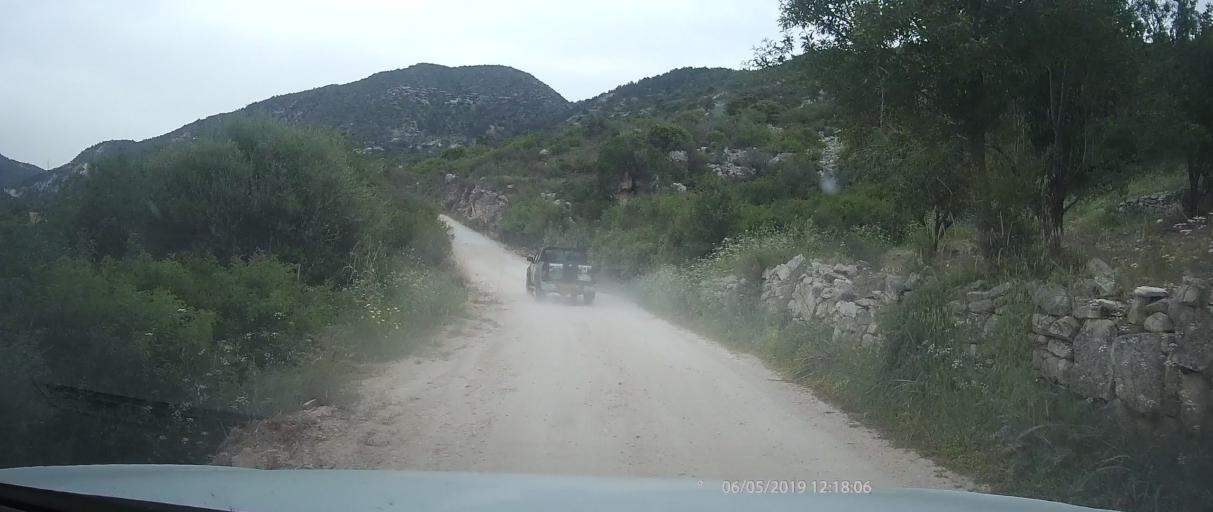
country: CY
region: Pafos
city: Tala
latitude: 34.8587
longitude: 32.4255
